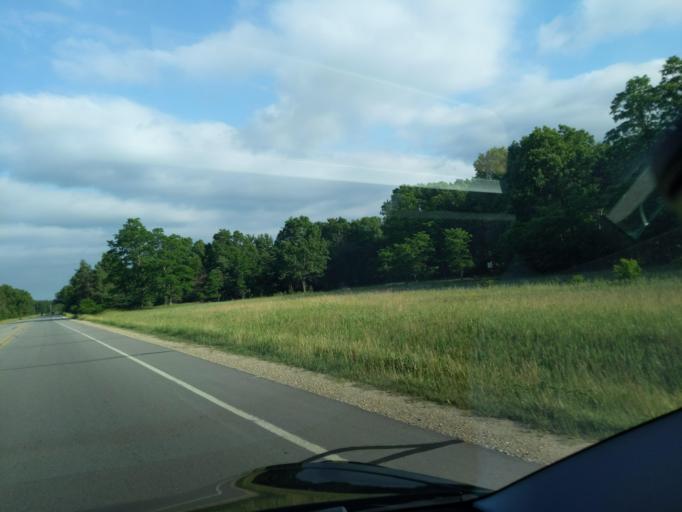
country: US
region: Michigan
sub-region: Muskegon County
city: Lakewood Club
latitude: 43.3912
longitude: -86.2968
